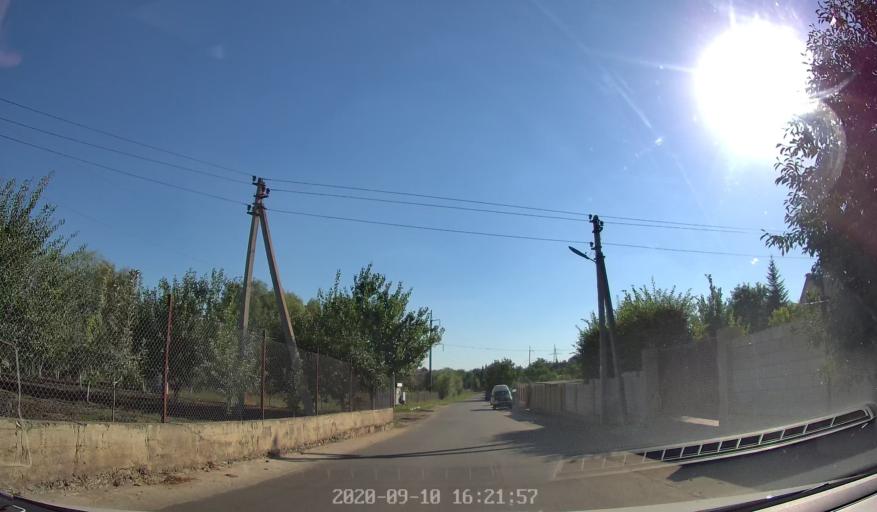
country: MD
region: Chisinau
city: Stauceni
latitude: 47.0553
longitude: 28.9260
